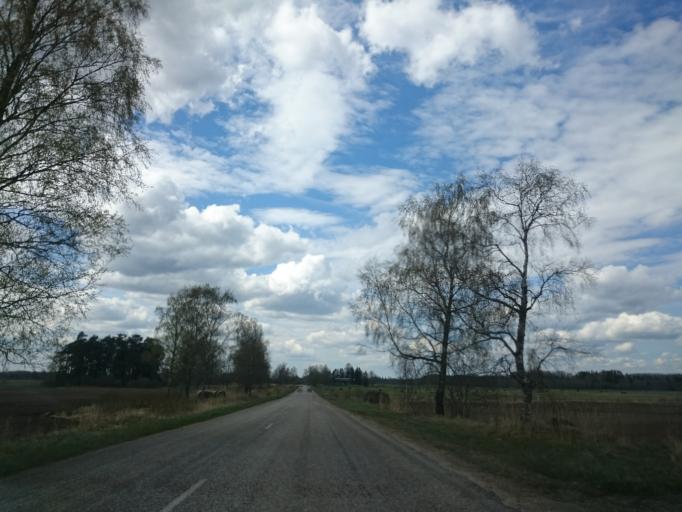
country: LV
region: Talsu Rajons
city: Sabile
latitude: 56.9503
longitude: 22.3448
